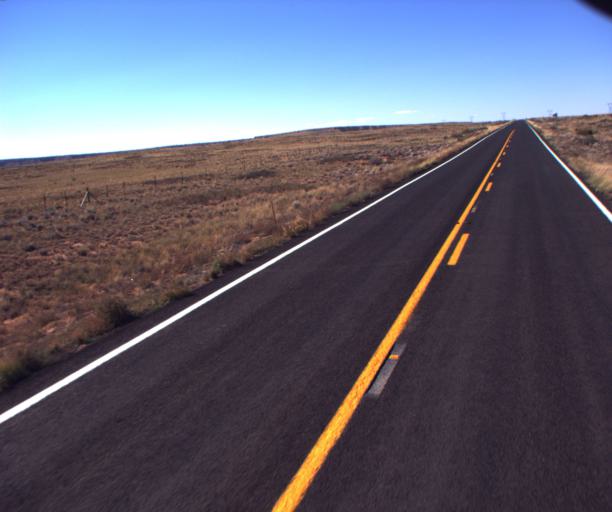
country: US
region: Arizona
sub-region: Navajo County
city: First Mesa
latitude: 35.9694
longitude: -110.8115
